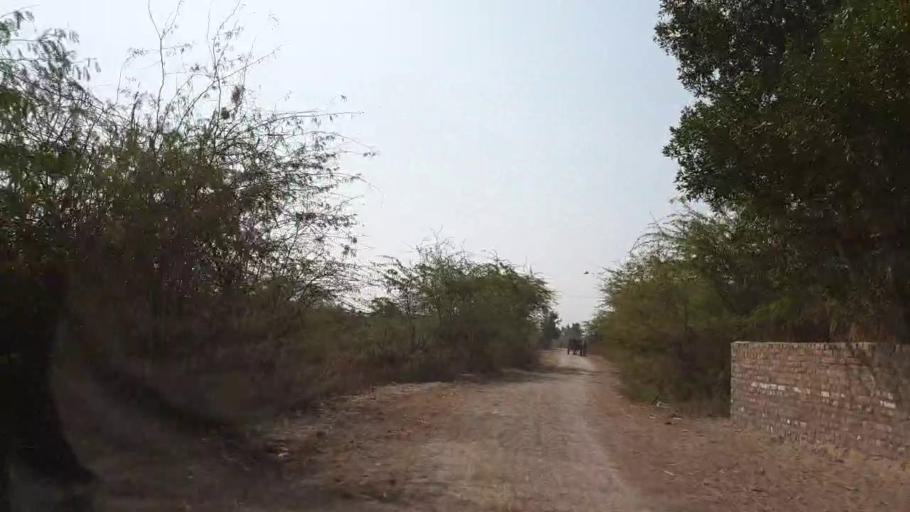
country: PK
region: Sindh
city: Mirpur Khas
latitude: 25.6042
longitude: 69.0220
